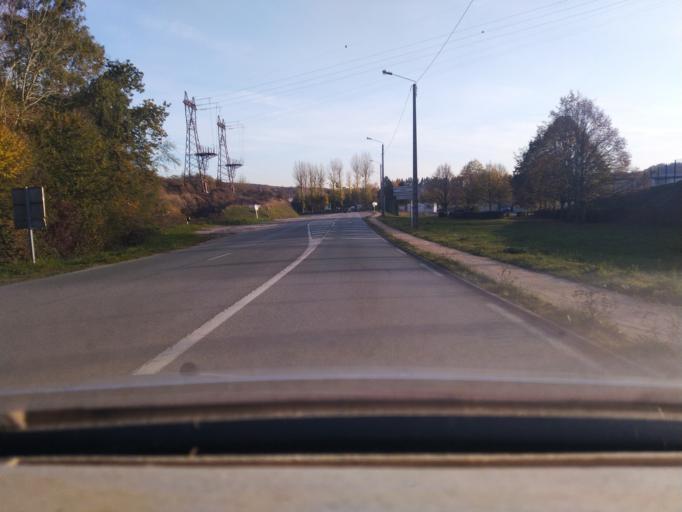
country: FR
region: Haute-Normandie
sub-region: Departement de la Seine-Maritime
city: Yainville
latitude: 49.4602
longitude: 0.8232
